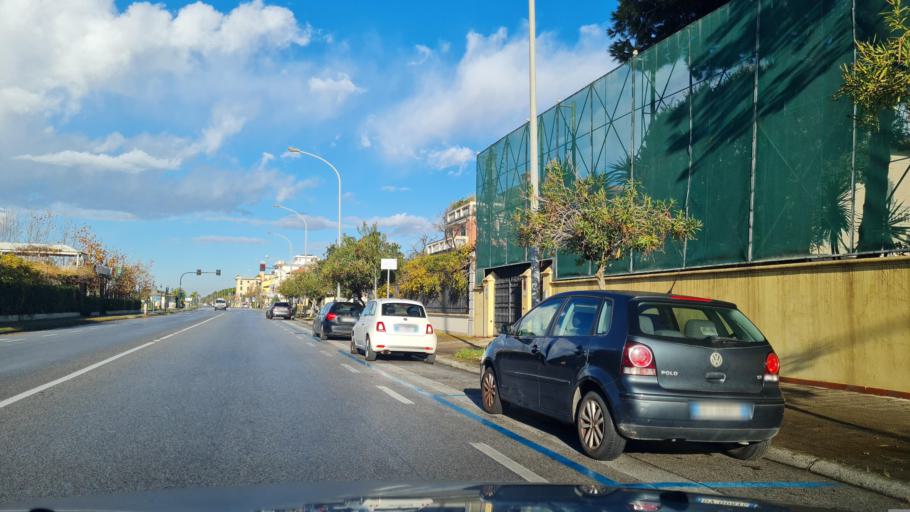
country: IT
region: Tuscany
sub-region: Provincia di Lucca
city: Pietrasanta
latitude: 43.9360
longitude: 10.1910
